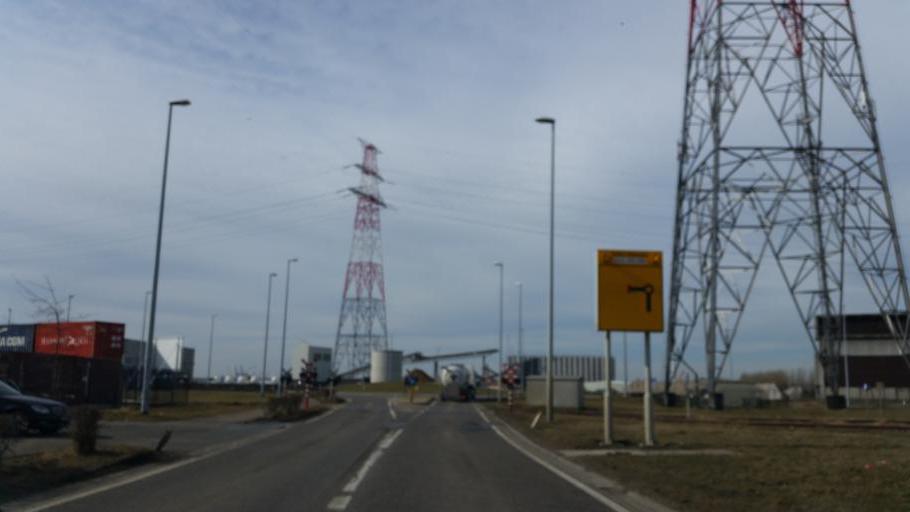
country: BE
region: Flanders
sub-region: Provincie Oost-Vlaanderen
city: Beveren
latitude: 51.2659
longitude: 4.2763
